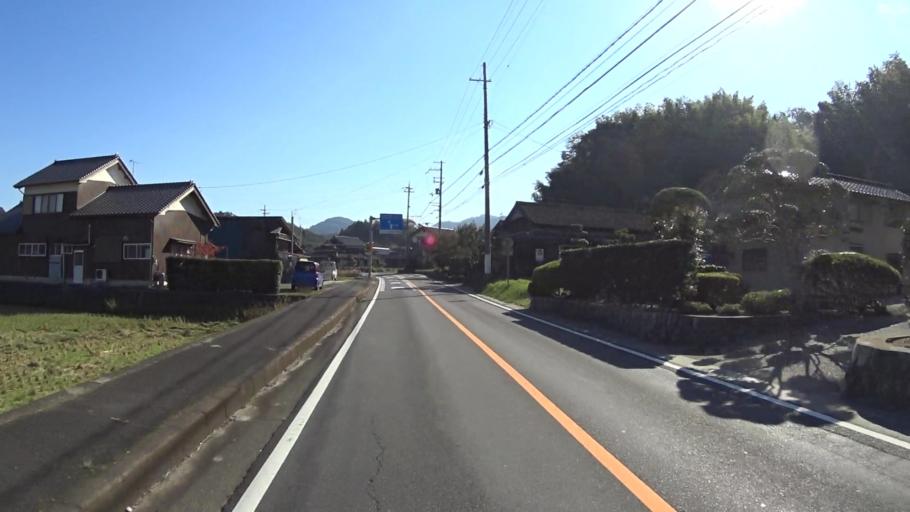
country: JP
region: Kyoto
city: Miyazu
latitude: 35.6536
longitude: 135.0321
